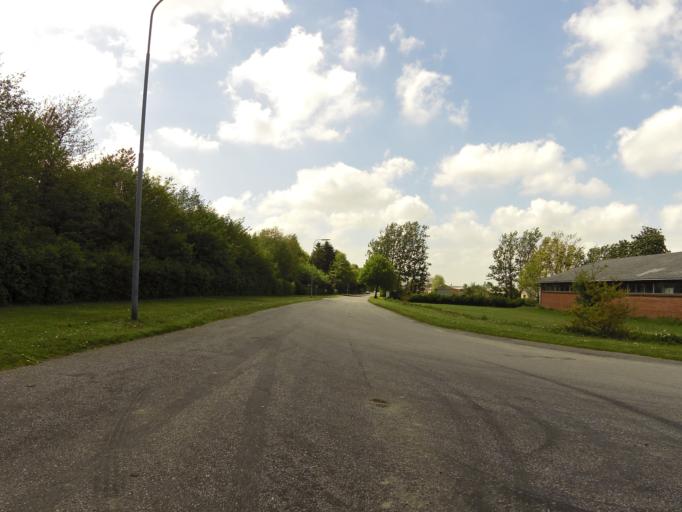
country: DK
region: South Denmark
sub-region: Tonder Kommune
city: Toftlund
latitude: 55.1887
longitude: 9.0867
